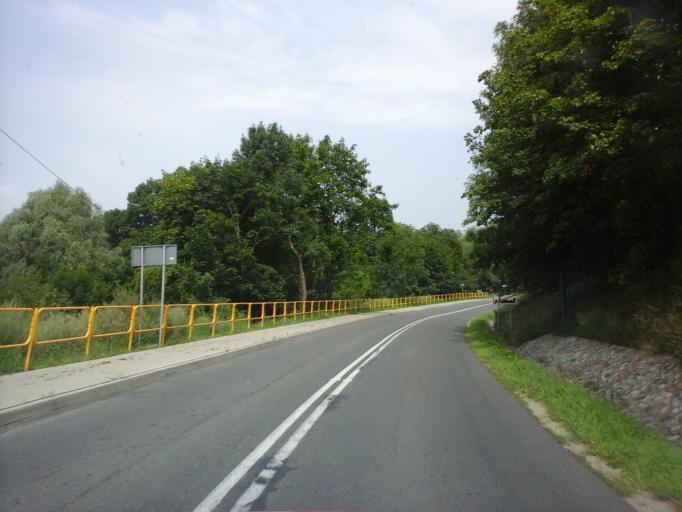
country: PL
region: West Pomeranian Voivodeship
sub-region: Powiat choszczenski
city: Pelczyce
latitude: 53.0476
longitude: 15.2992
